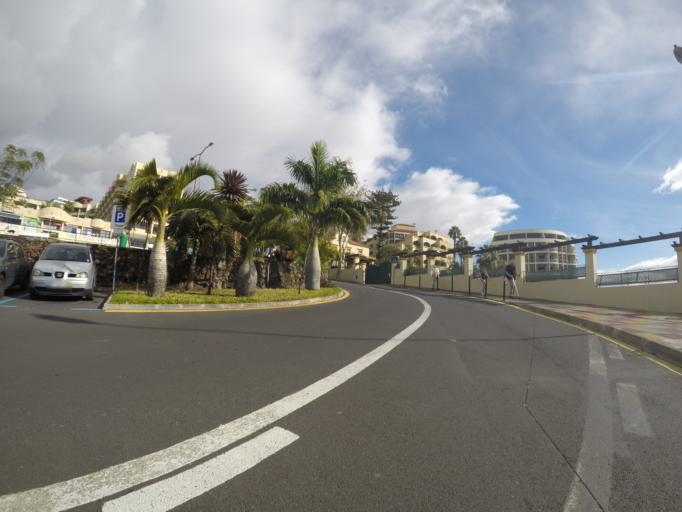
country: PT
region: Madeira
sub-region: Funchal
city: Funchal
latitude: 32.6363
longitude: -16.9317
